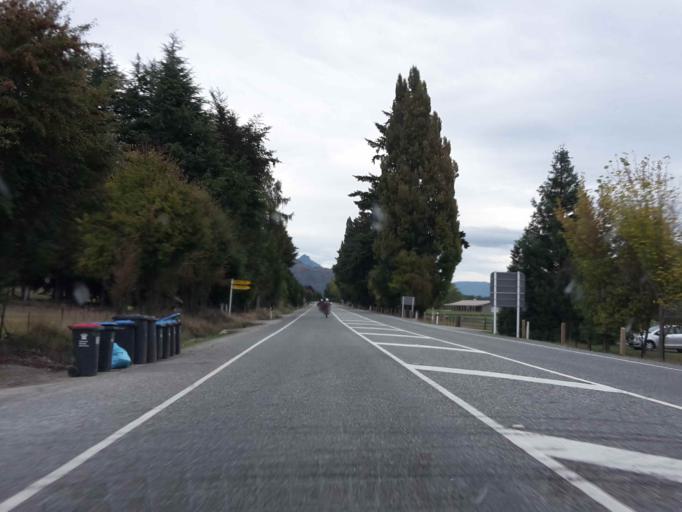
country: NZ
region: Otago
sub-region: Queenstown-Lakes District
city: Arrowtown
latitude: -44.9886
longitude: 168.8133
